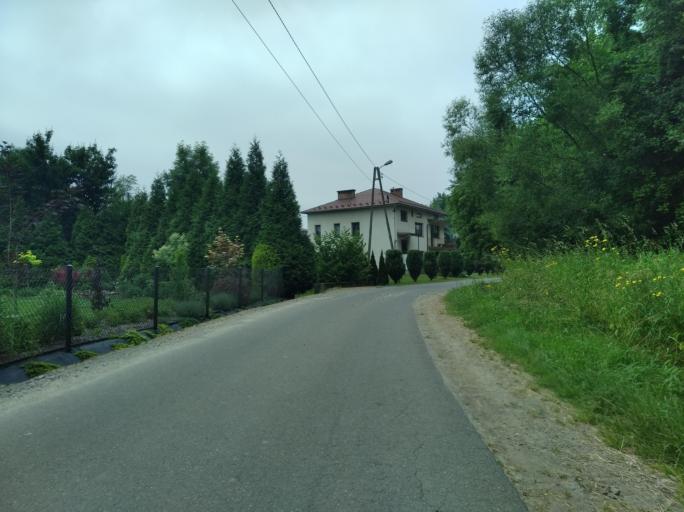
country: PL
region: Subcarpathian Voivodeship
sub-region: Powiat brzozowski
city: Haczow
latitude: 49.6757
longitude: 21.8932
